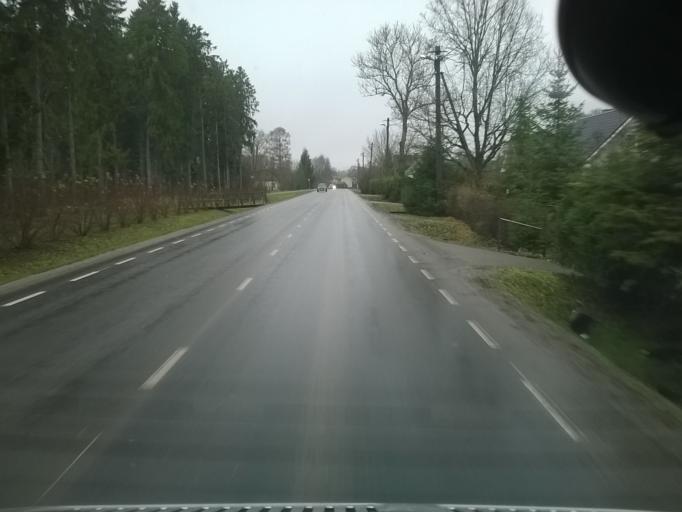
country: EE
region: Harju
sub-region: Saku vald
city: Saku
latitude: 59.2368
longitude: 24.6824
